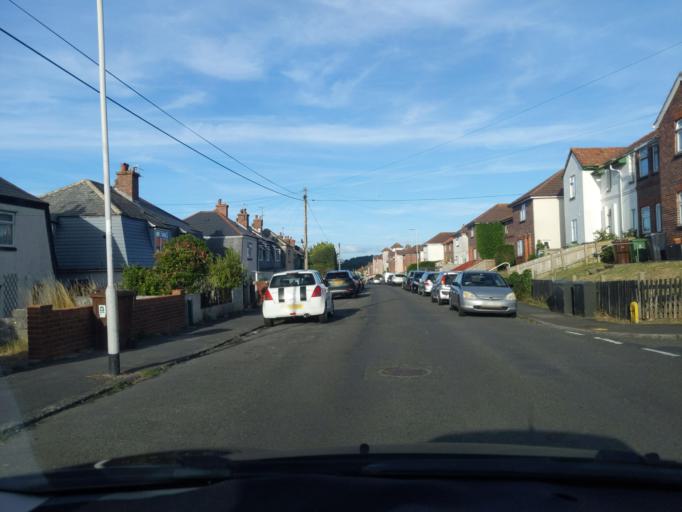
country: GB
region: England
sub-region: Plymouth
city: Plymouth
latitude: 50.3794
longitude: -4.1160
